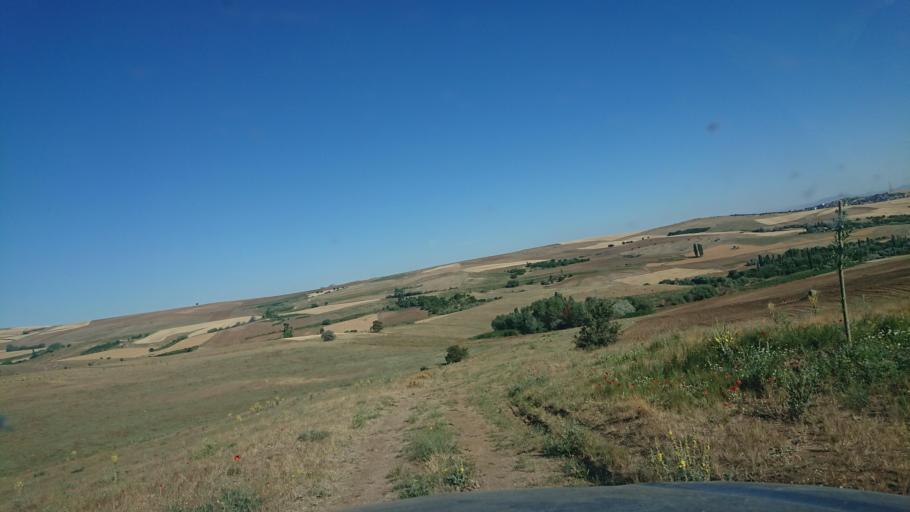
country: TR
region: Aksaray
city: Agacoren
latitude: 38.8399
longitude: 33.9331
